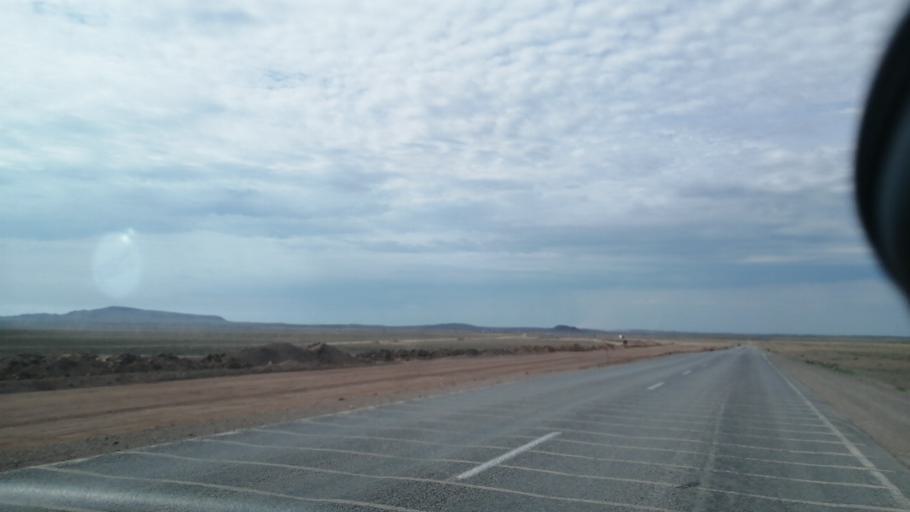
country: KZ
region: Qaraghandy
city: Balqash
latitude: 46.6785
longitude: 74.4210
